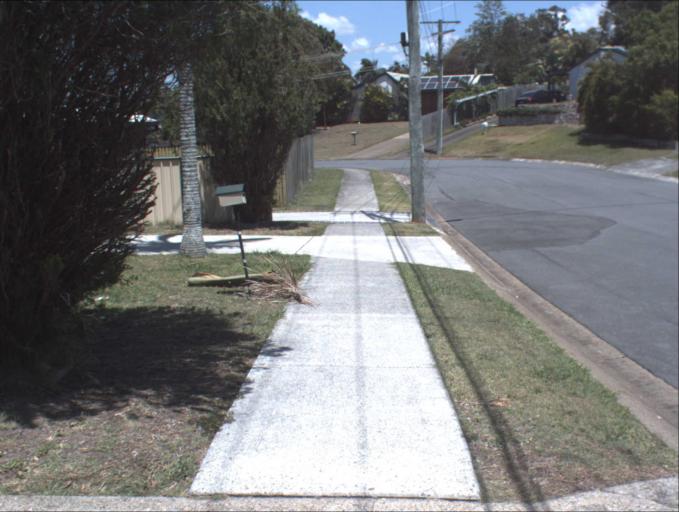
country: AU
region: Queensland
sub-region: Logan
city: Springwood
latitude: -27.5992
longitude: 153.1396
